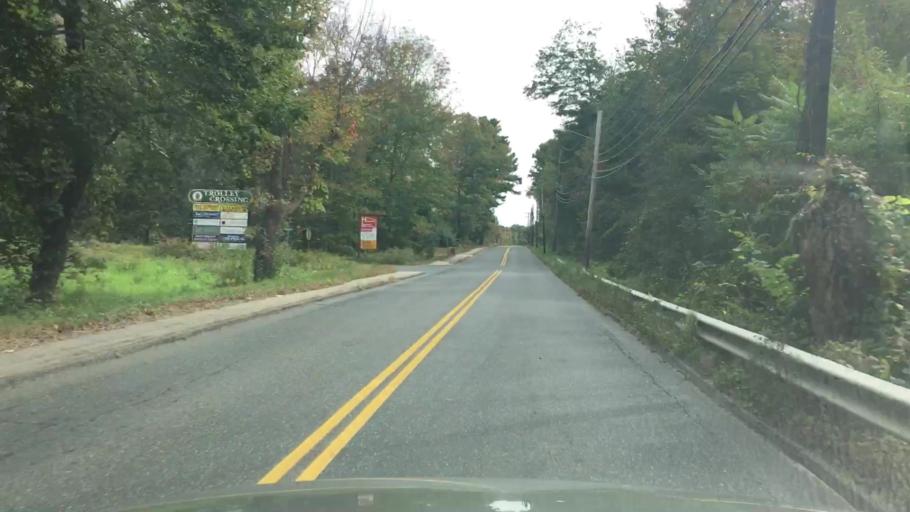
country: US
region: Massachusetts
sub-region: Worcester County
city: Charlton
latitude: 42.1437
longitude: -71.9837
